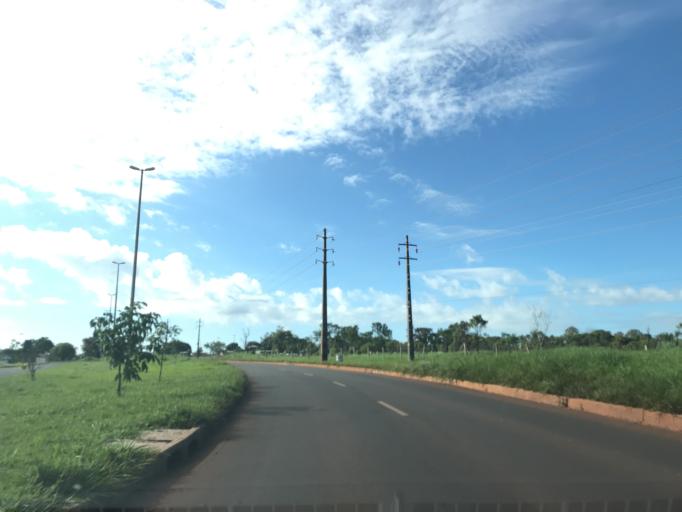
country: BR
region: Federal District
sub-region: Brasilia
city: Brasilia
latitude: -15.7660
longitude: -47.8990
